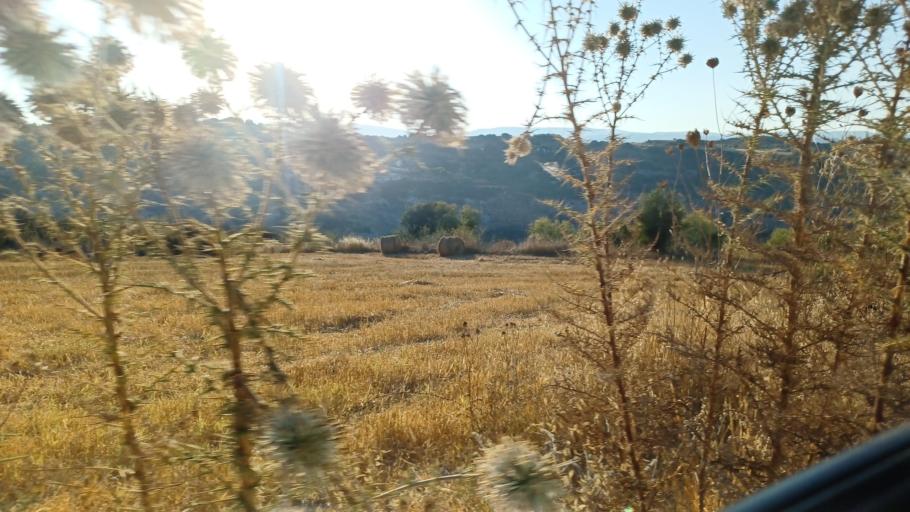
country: CY
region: Pafos
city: Mesogi
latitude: 34.8774
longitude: 32.5291
